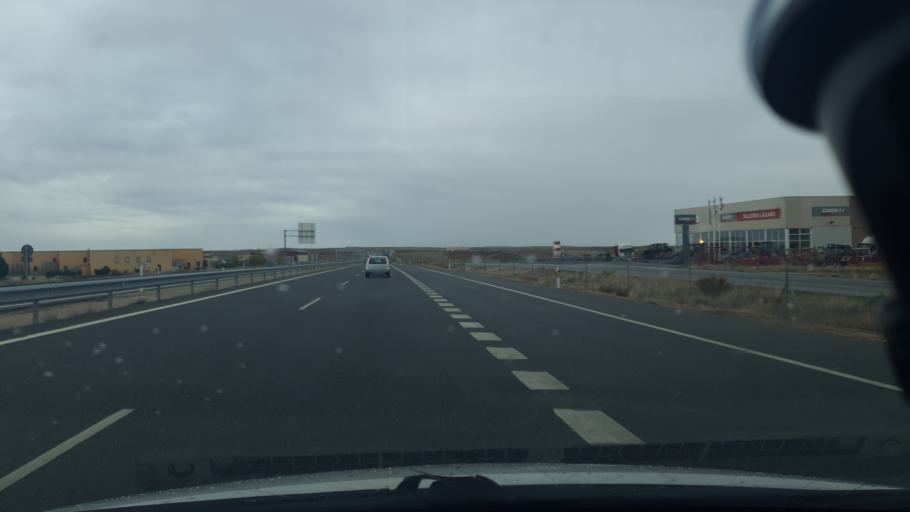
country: ES
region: Castille and Leon
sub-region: Provincia de Segovia
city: Encinillas
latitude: 41.0042
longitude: -4.1561
